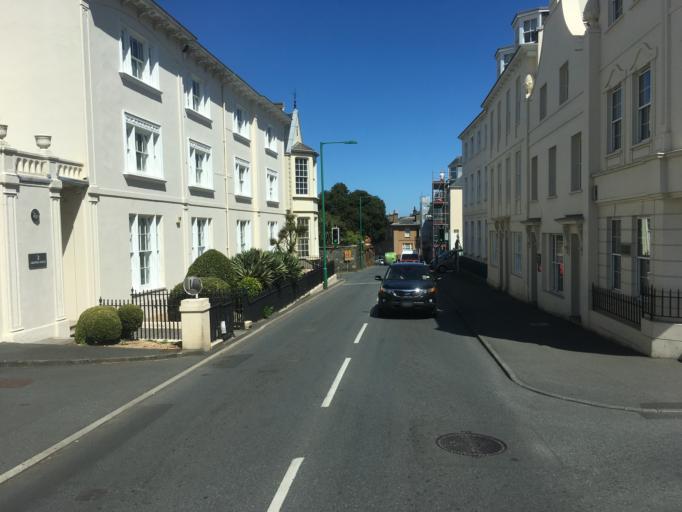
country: GG
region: St Peter Port
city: Saint Peter Port
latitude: 49.4561
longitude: -2.5414
